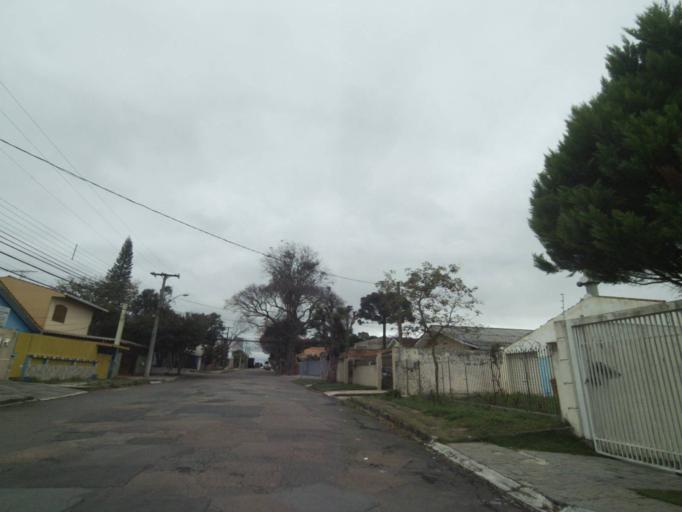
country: BR
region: Parana
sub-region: Curitiba
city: Curitiba
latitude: -25.4994
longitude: -49.2997
